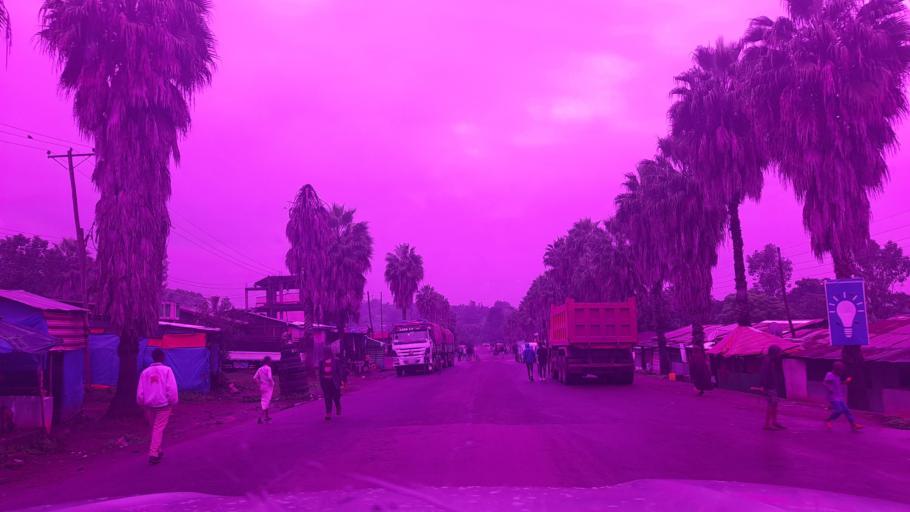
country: ET
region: Oromiya
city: Jima
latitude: 7.8435
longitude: 37.3680
